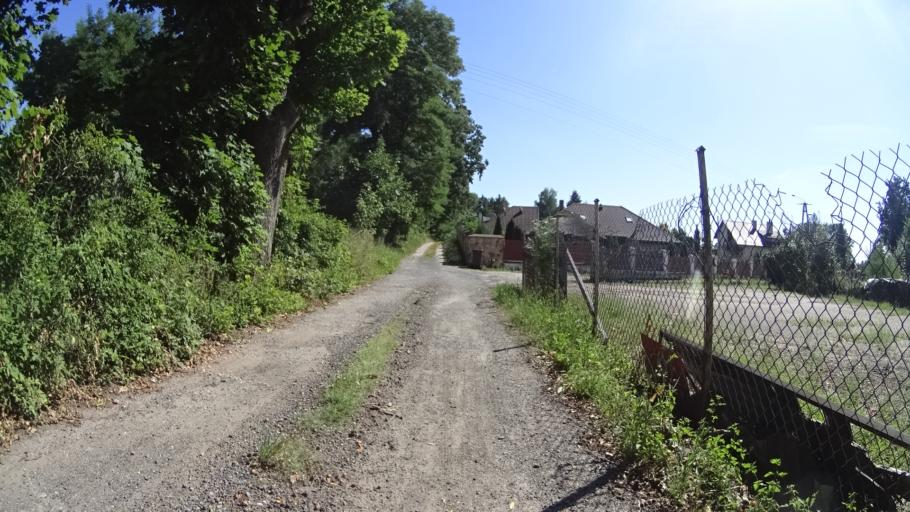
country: PL
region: Masovian Voivodeship
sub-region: Powiat bialobrzeski
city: Bialobrzegi
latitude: 51.6693
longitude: 20.9211
